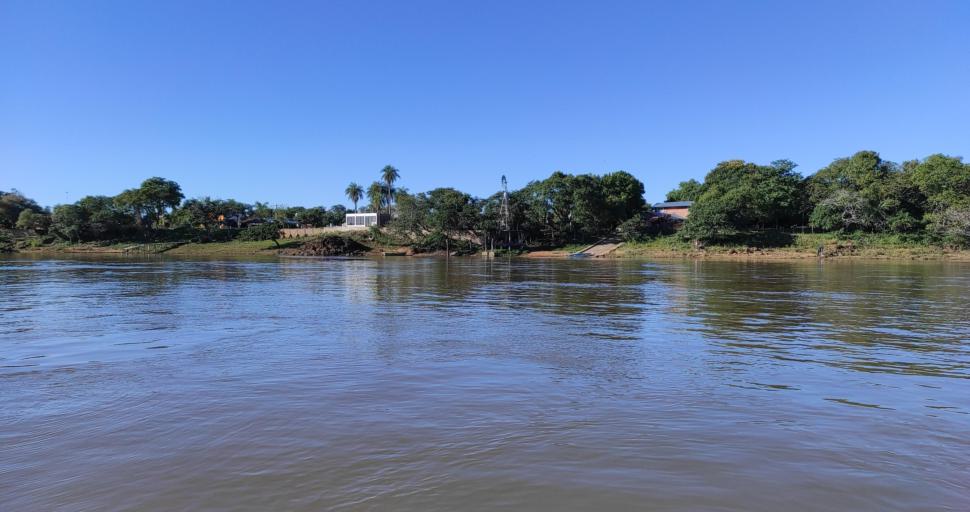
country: AR
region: Corrientes
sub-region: Departamento de Itati
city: Itati
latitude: -27.2644
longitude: -58.2690
